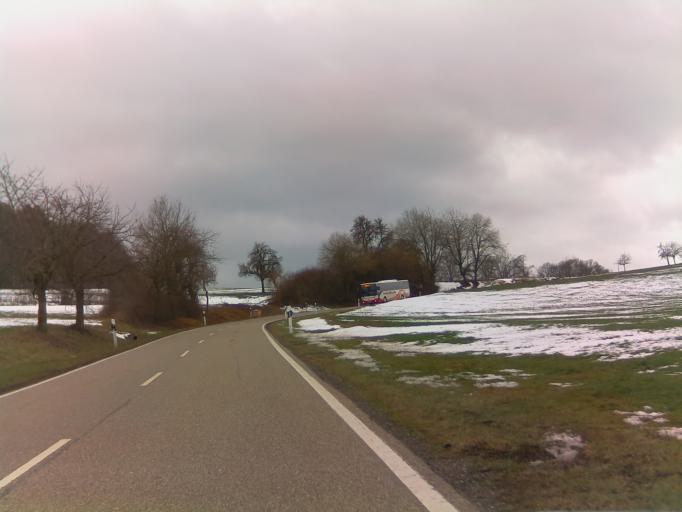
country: DE
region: Hesse
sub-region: Regierungsbezirk Darmstadt
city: Erbach
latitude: 49.6774
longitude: 8.9470
